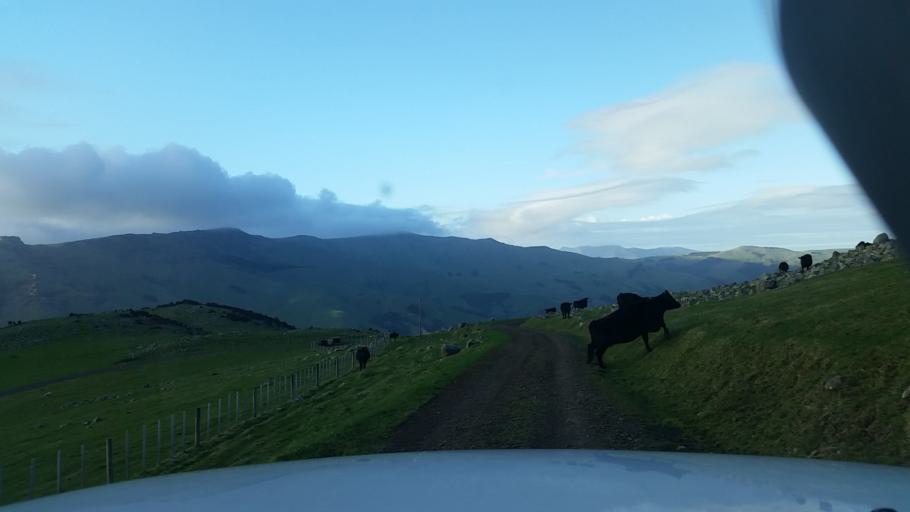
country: NZ
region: Canterbury
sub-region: Christchurch City
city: Christchurch
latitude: -43.6579
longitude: 172.8782
